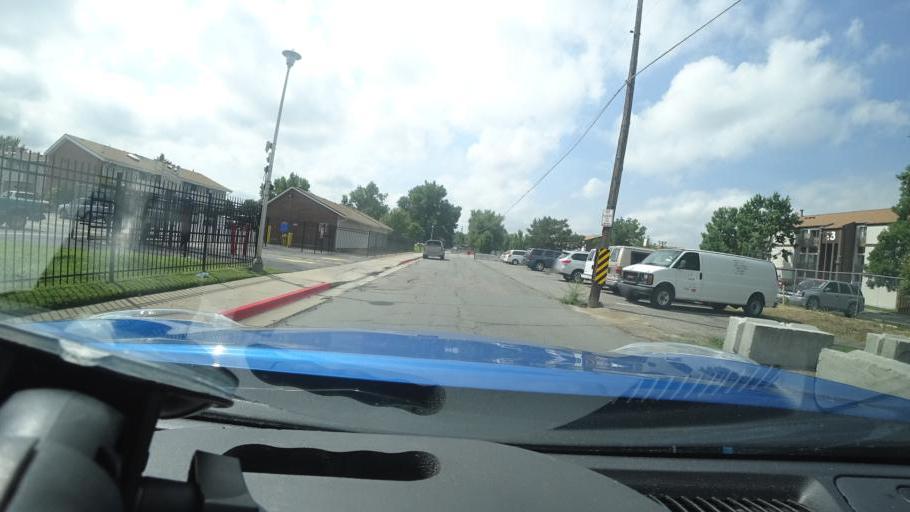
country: US
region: Colorado
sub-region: Adams County
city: Aurora
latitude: 39.7062
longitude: -104.8706
